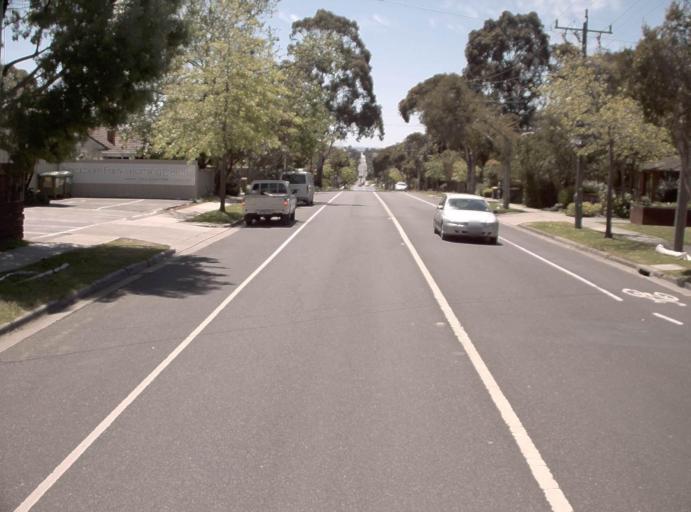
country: AU
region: Victoria
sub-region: Whitehorse
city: Blackburn North
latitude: -37.8101
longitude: 145.1579
